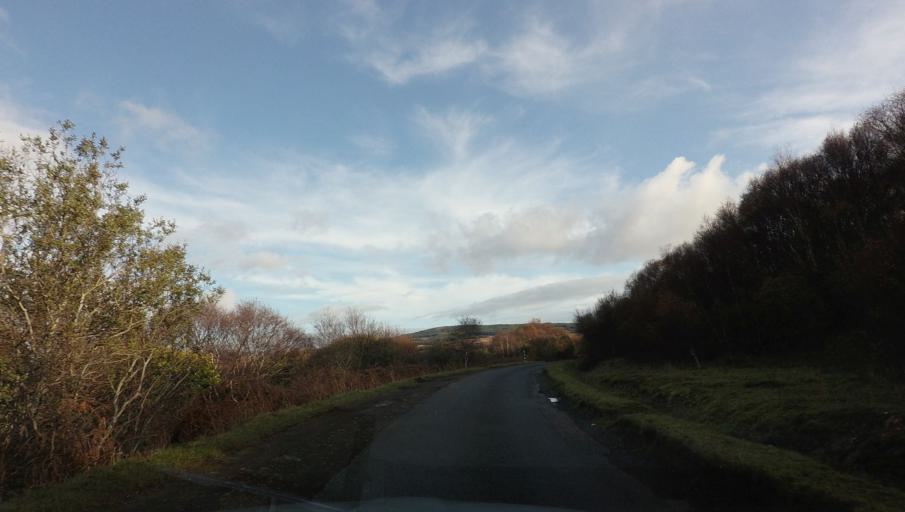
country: GB
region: Scotland
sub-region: Argyll and Bute
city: Isle Of Mull
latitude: 56.3437
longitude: -6.1093
